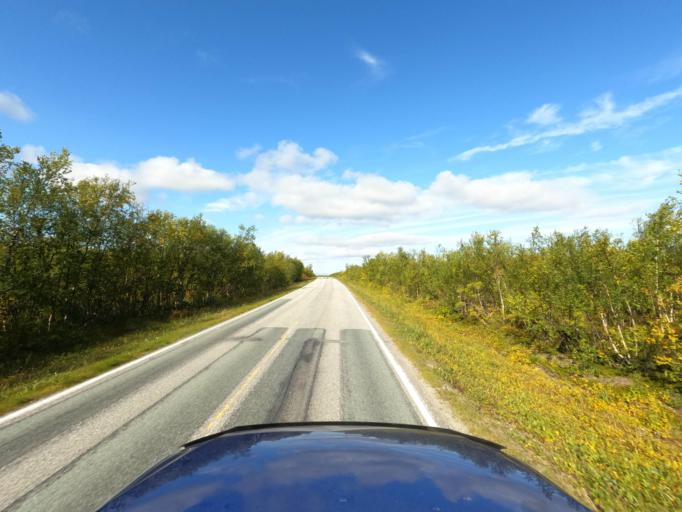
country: NO
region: Finnmark Fylke
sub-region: Karasjok
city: Karasjohka
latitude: 69.5870
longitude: 25.3449
